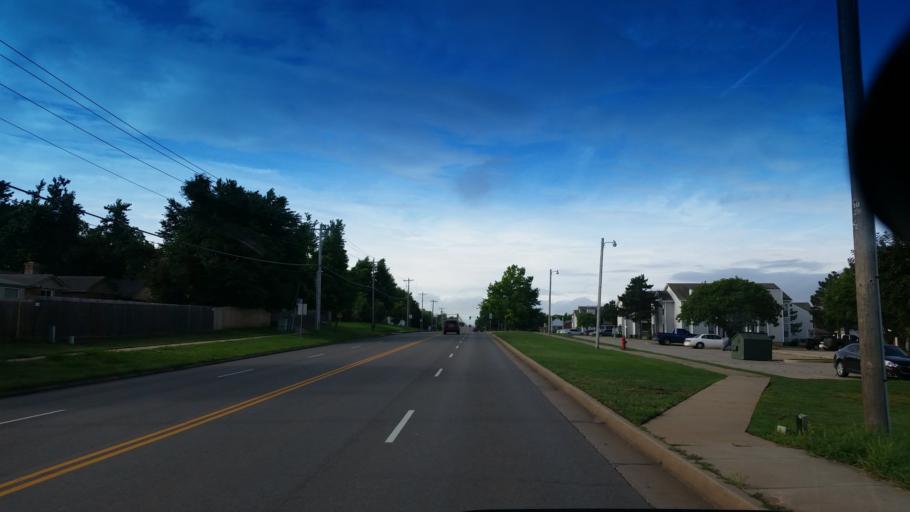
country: US
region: Oklahoma
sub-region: Oklahoma County
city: Edmond
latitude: 35.6632
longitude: -97.4961
